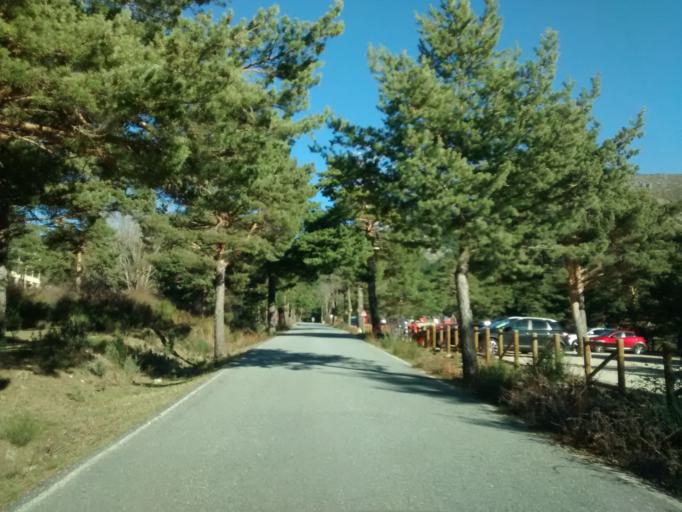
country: ES
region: Madrid
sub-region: Provincia de Madrid
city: Navacerrada
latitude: 40.7510
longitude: -3.9933
